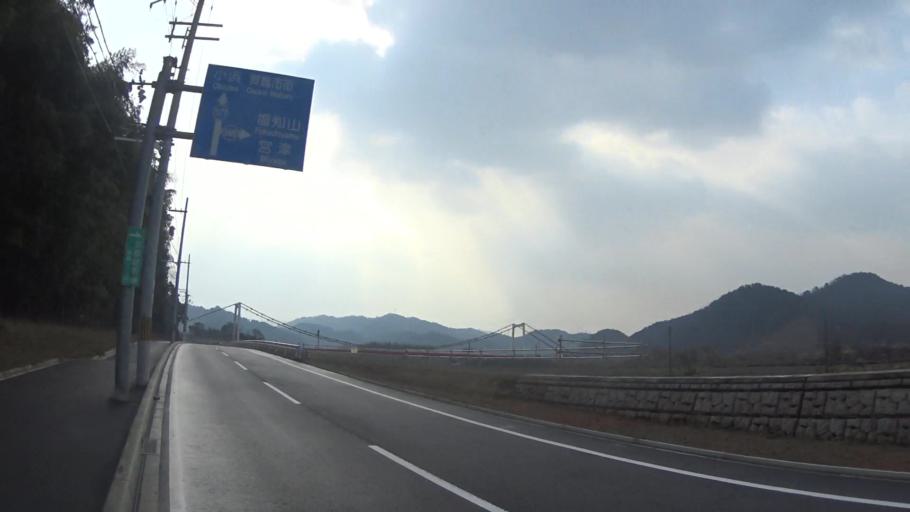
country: JP
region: Kyoto
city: Maizuru
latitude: 35.4686
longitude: 135.2829
